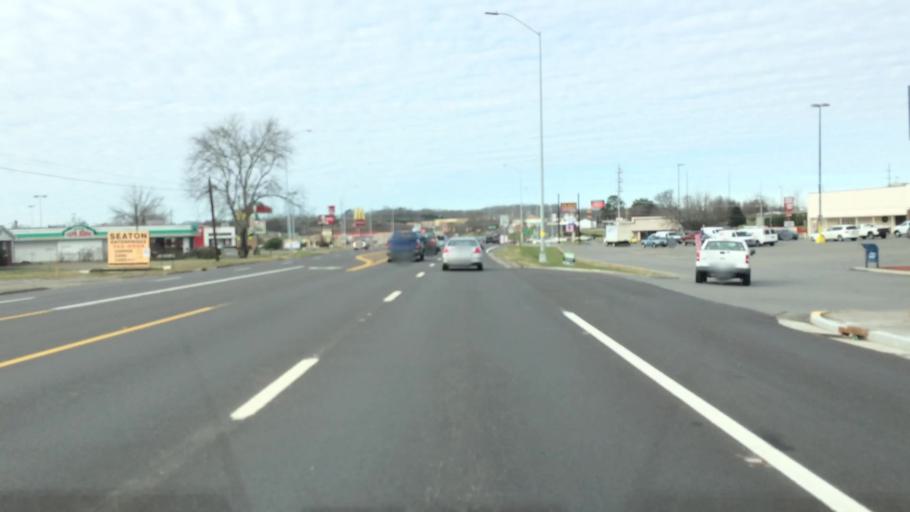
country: US
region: Tennessee
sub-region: McMinn County
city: Athens
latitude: 35.4501
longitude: -84.6201
